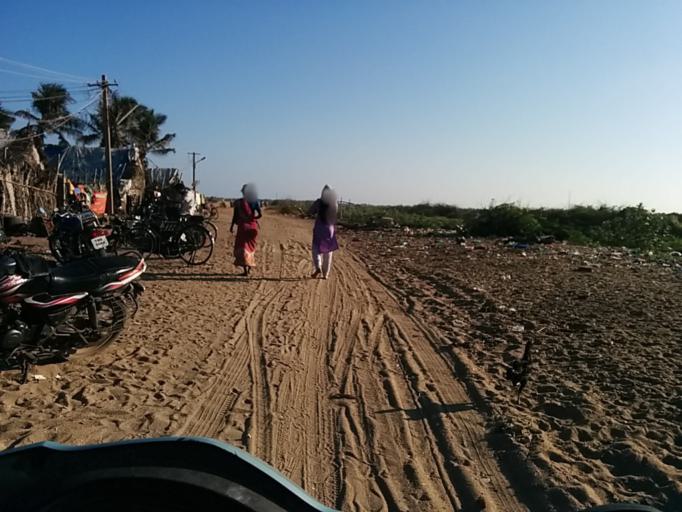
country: IN
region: Pondicherry
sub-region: Puducherry
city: Puducherry
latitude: 11.9148
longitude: 79.8300
